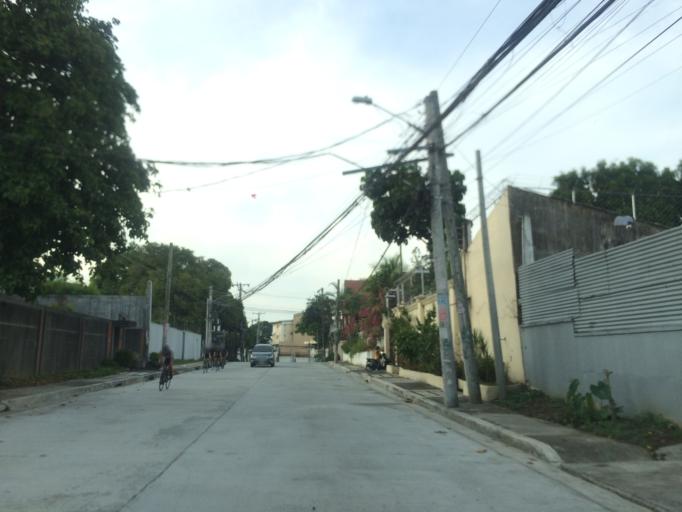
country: PH
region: Calabarzon
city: Del Monte
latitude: 14.6299
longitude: 121.0059
